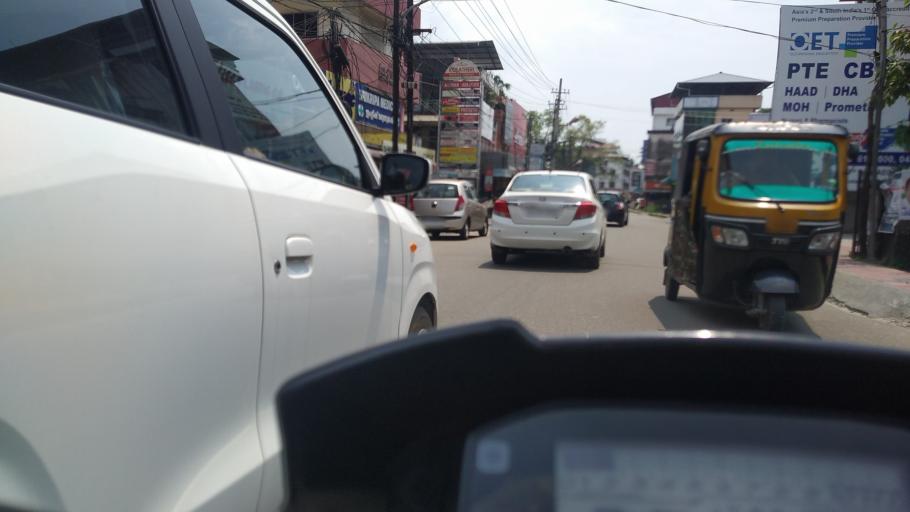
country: IN
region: Kerala
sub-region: Ernakulam
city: Cochin
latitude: 9.9662
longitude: 76.2884
